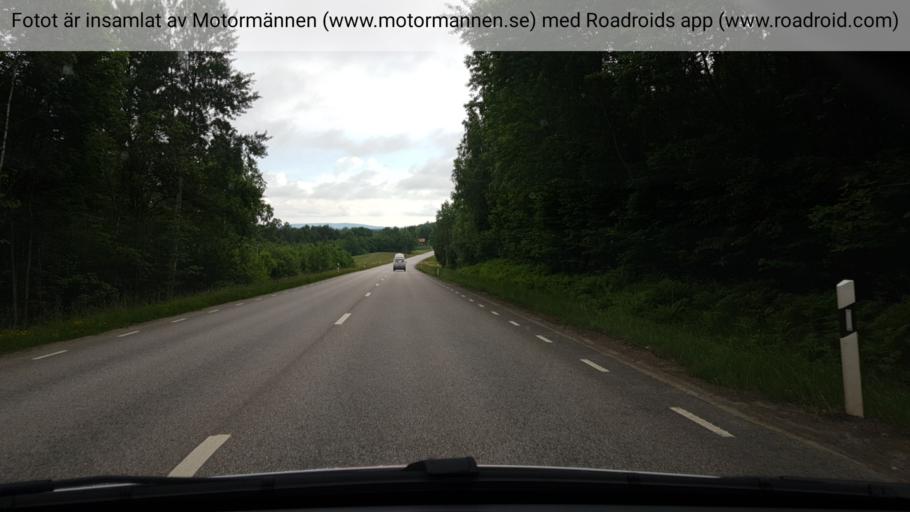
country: SE
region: Vaestra Goetaland
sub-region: Karlsborgs Kommun
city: Molltorp
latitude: 58.4624
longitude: 14.2870
